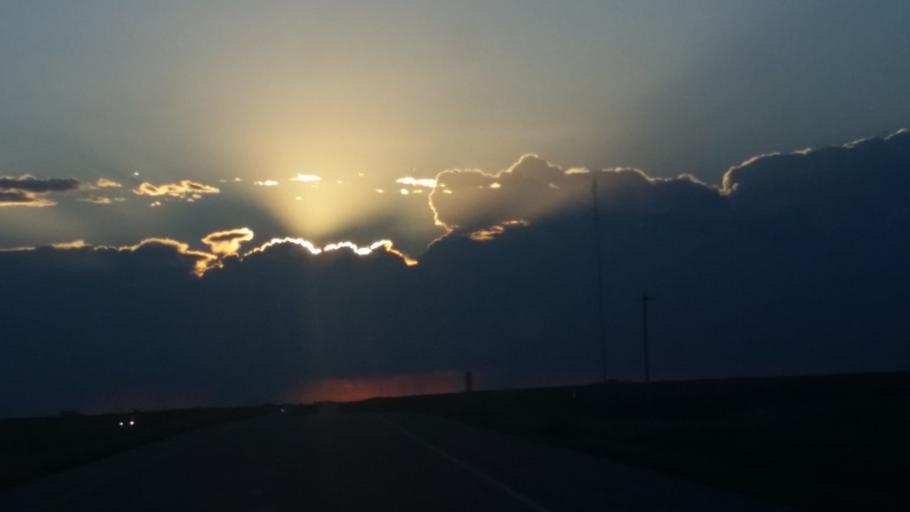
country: US
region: Kansas
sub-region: Ellsworth County
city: Ellsworth
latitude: 38.8481
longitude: -98.2097
